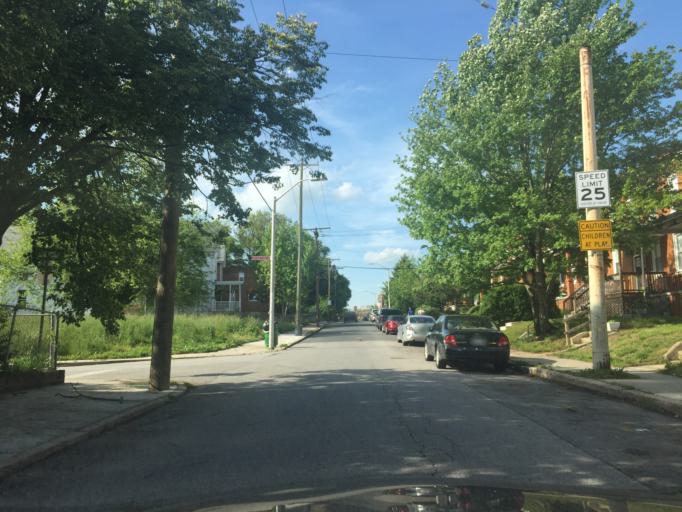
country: US
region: Maryland
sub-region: City of Baltimore
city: Baltimore
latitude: 39.3324
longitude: -76.6078
